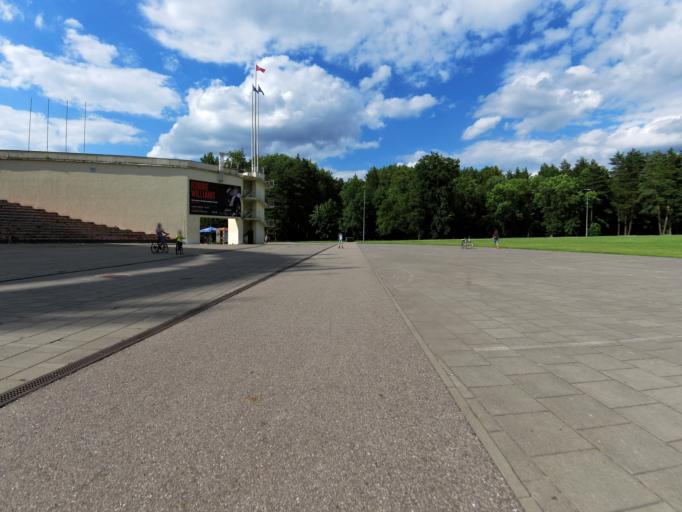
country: LT
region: Vilnius County
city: Vilkpede
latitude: 54.6831
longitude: 25.2367
